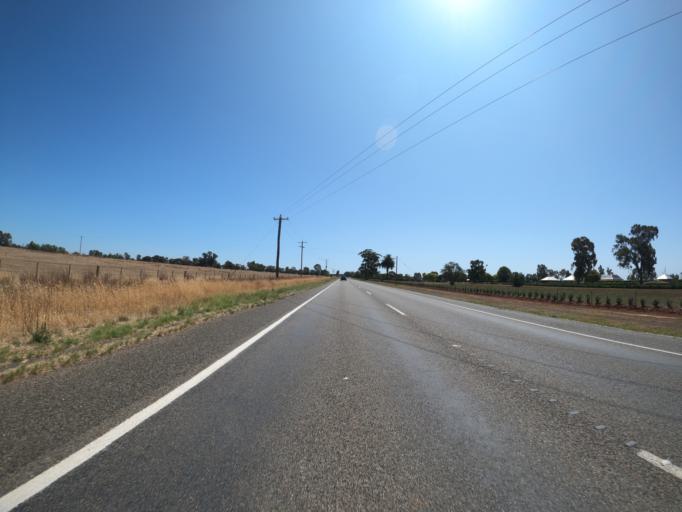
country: AU
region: Victoria
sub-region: Moira
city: Yarrawonga
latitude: -36.0263
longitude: 146.0891
